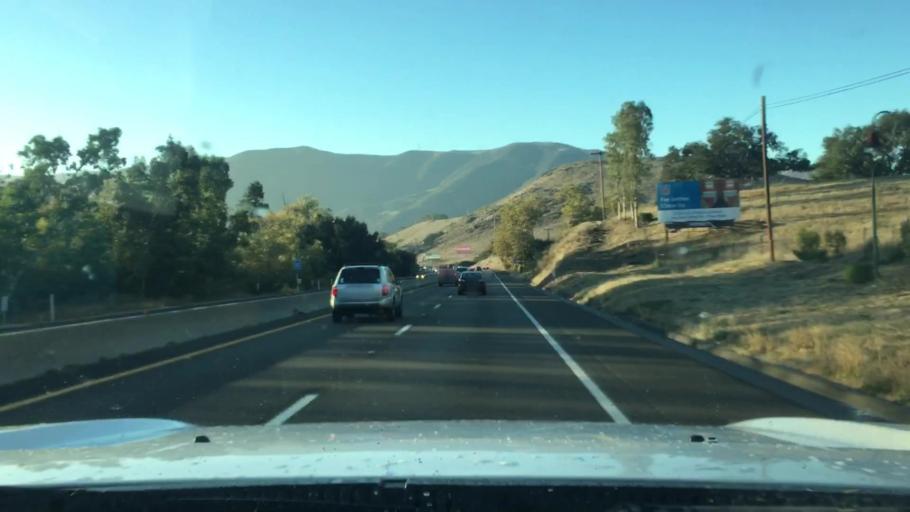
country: US
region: California
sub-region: San Luis Obispo County
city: San Luis Obispo
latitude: 35.3078
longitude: -120.6252
